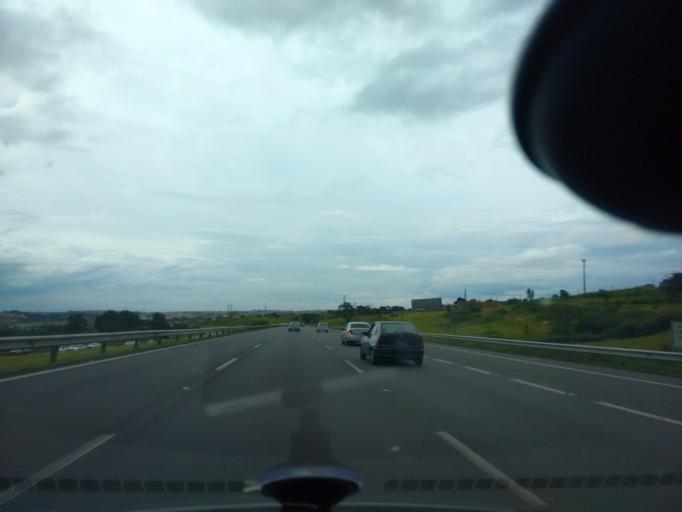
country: BR
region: Sao Paulo
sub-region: Campinas
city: Campinas
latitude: -22.9829
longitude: -47.1114
